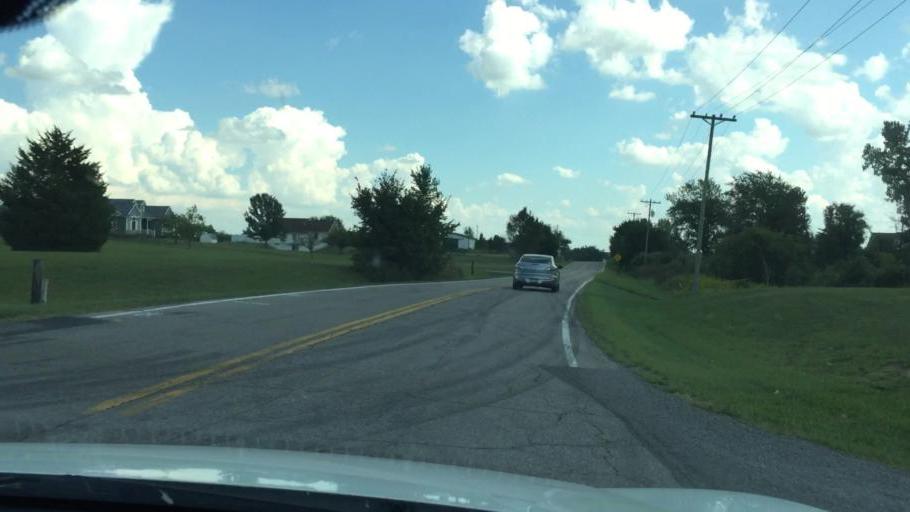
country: US
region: Ohio
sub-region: Champaign County
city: North Lewisburg
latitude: 40.2569
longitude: -83.4898
